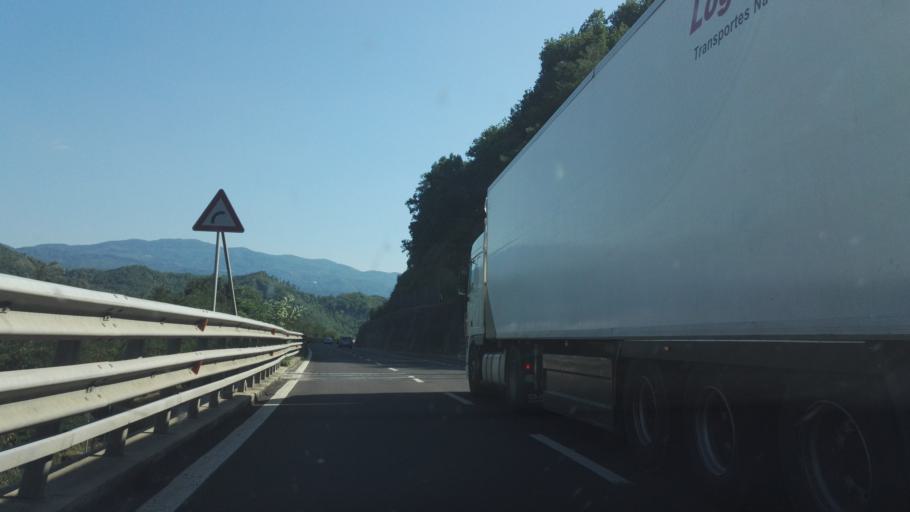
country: IT
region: Calabria
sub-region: Provincia di Cosenza
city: Altilia
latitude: 39.1418
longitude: 16.2744
